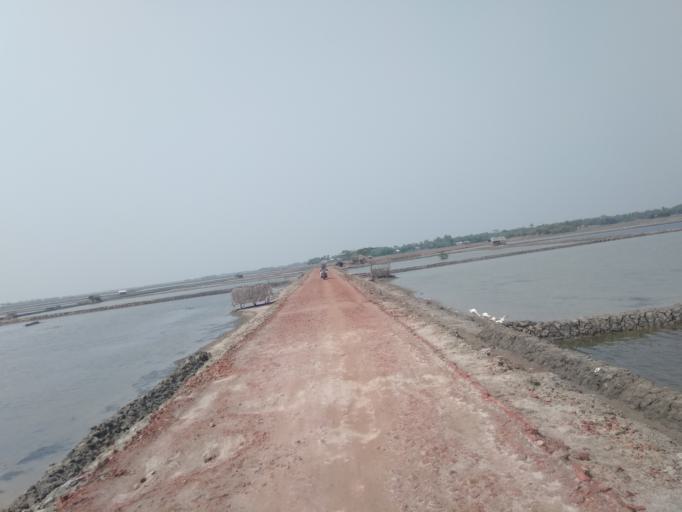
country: IN
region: West Bengal
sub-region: North 24 Parganas
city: Taki
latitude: 22.2917
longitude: 89.2716
